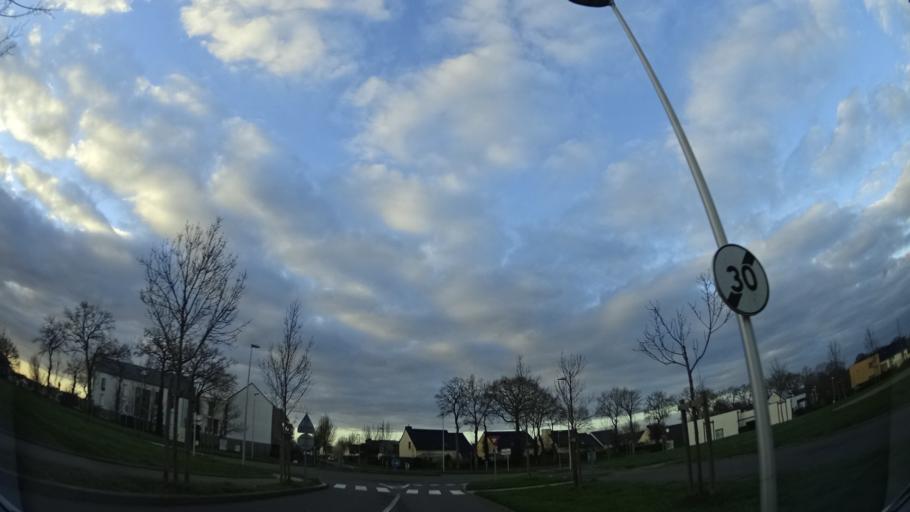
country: FR
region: Brittany
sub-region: Departement d'Ille-et-Vilaine
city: Betton
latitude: 48.1788
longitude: -1.6609
